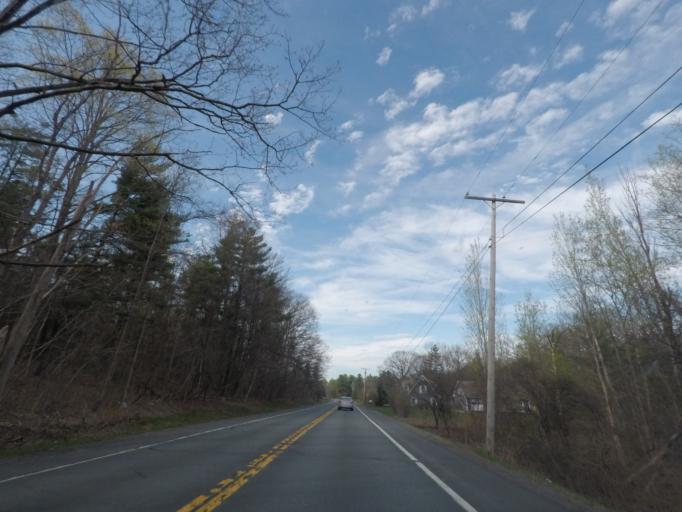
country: US
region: New York
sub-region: Albany County
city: Voorheesville
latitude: 42.6051
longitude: -73.9720
